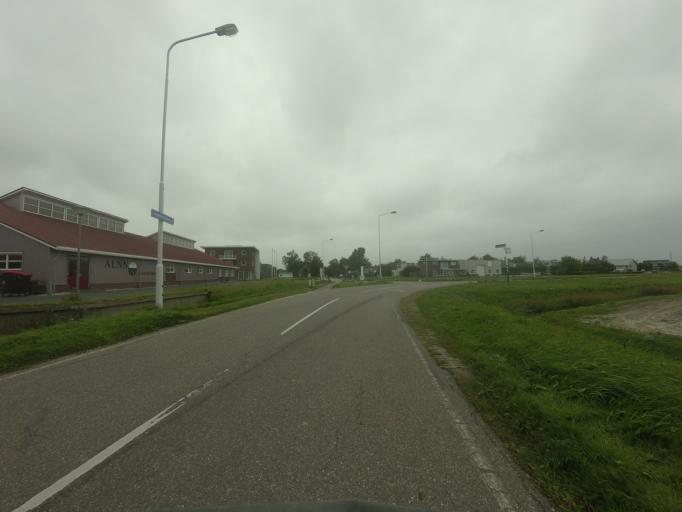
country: NL
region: Friesland
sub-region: Gemeente Ferwerderadiel
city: Ferwert
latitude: 53.3359
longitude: 5.8379
